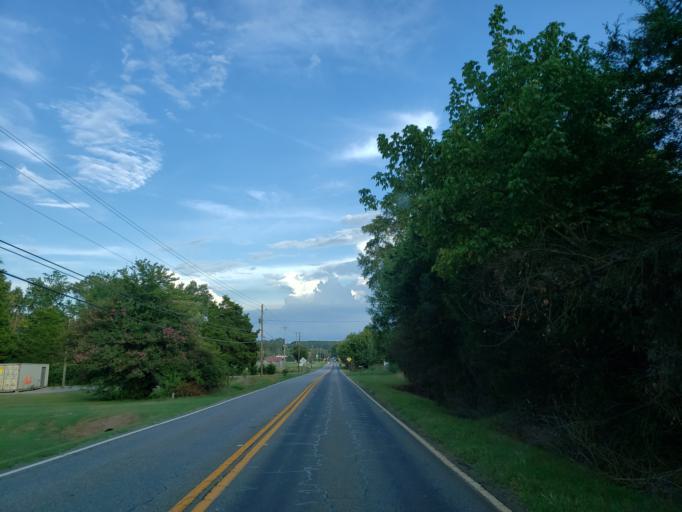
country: US
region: Georgia
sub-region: Bartow County
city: Cartersville
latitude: 34.2354
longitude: -84.8697
